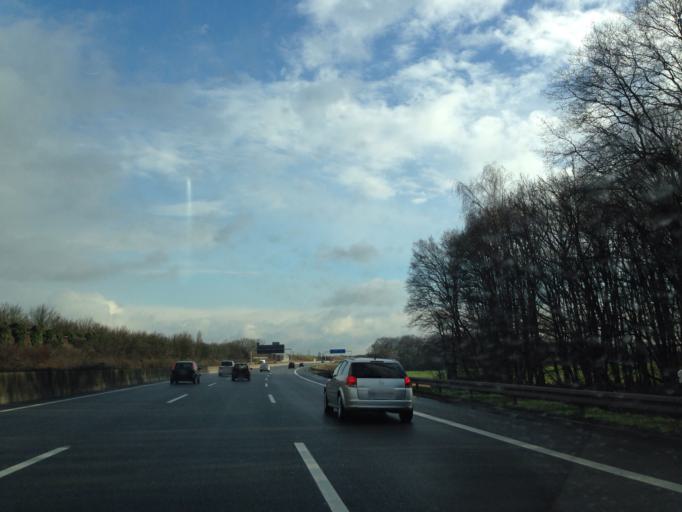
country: DE
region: North Rhine-Westphalia
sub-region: Regierungsbezirk Dusseldorf
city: Meerbusch
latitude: 51.2763
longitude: 6.6418
